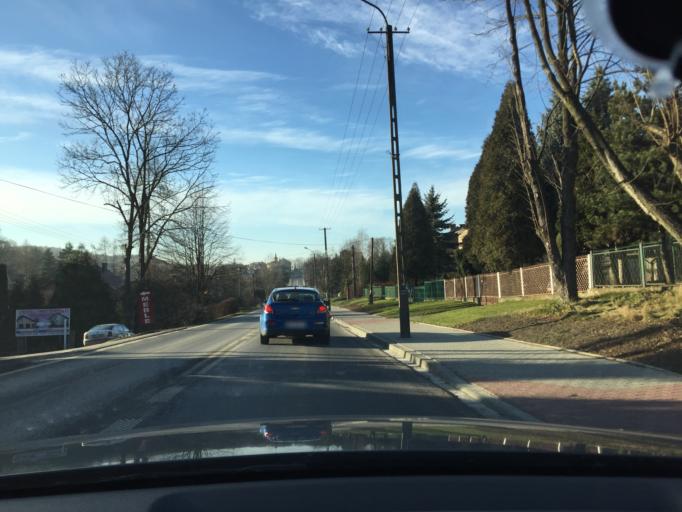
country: PL
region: Lesser Poland Voivodeship
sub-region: Powiat wadowicki
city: Kalwaria Zebrzydowska
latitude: 49.8665
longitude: 19.6859
